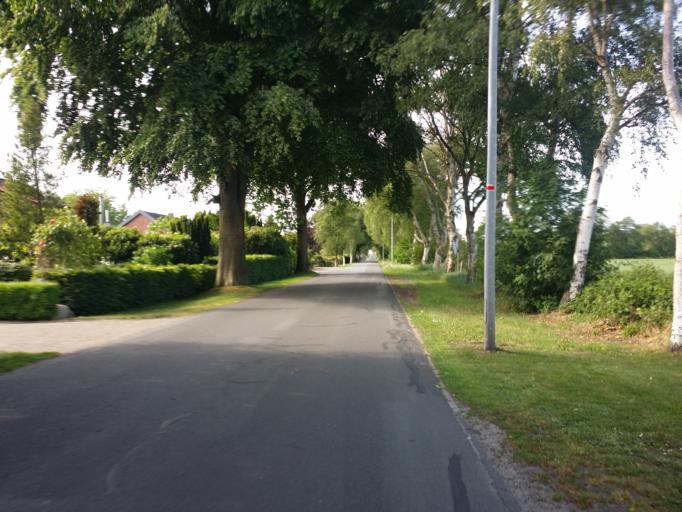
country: DE
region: Lower Saxony
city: Bockhorn
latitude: 53.3408
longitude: 8.0307
